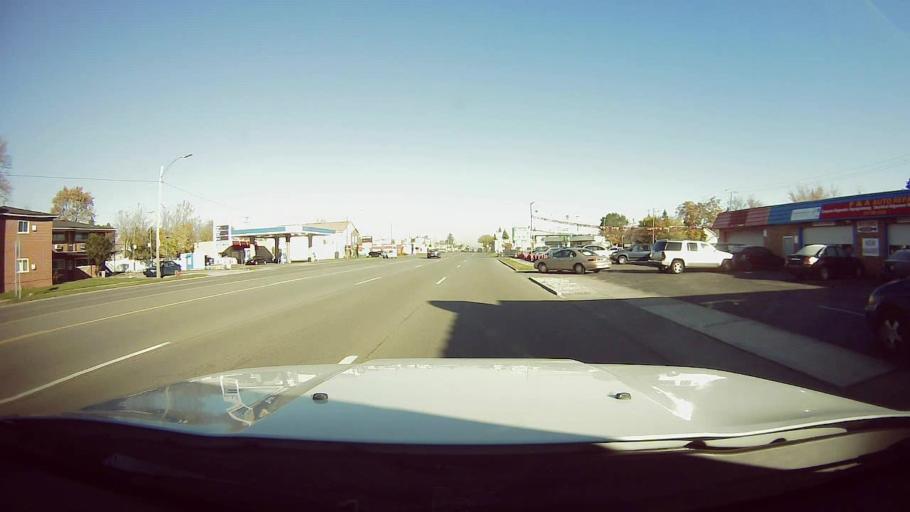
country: US
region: Michigan
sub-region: Wayne County
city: Dearborn
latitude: 42.3412
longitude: -83.1961
